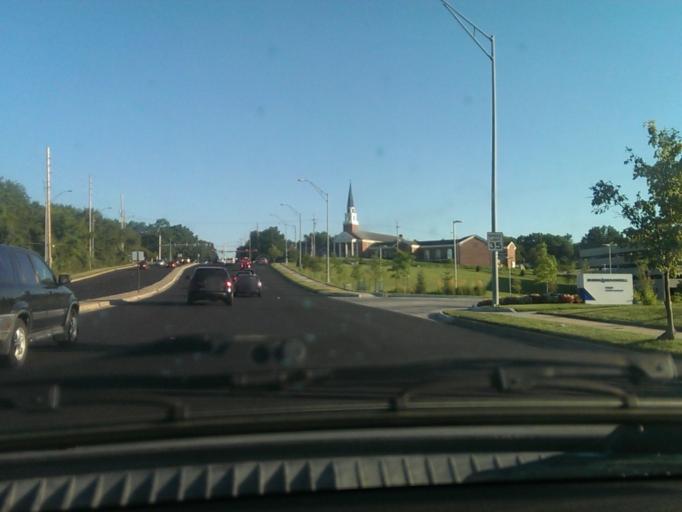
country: US
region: Kansas
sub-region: Johnson County
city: Leawood
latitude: 38.9581
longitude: -94.5958
